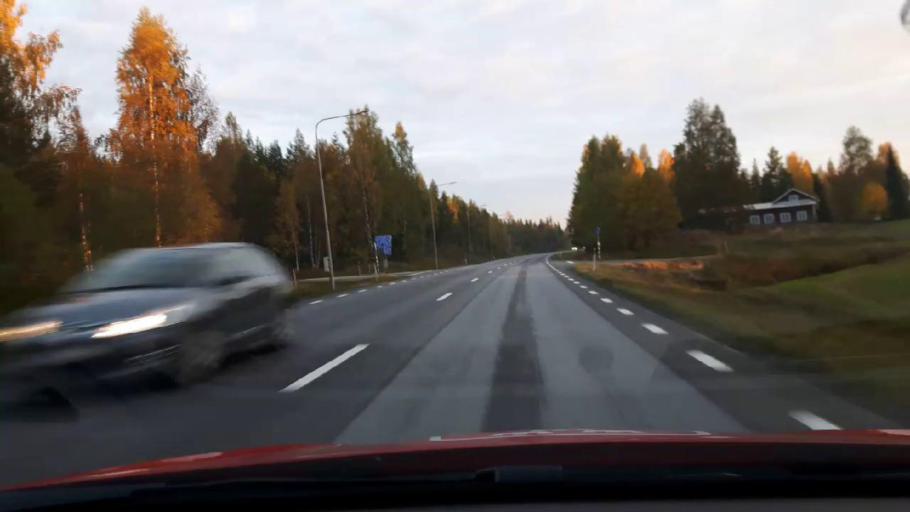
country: SE
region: Jaemtland
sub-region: OEstersunds Kommun
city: Lit
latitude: 63.3088
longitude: 14.8706
